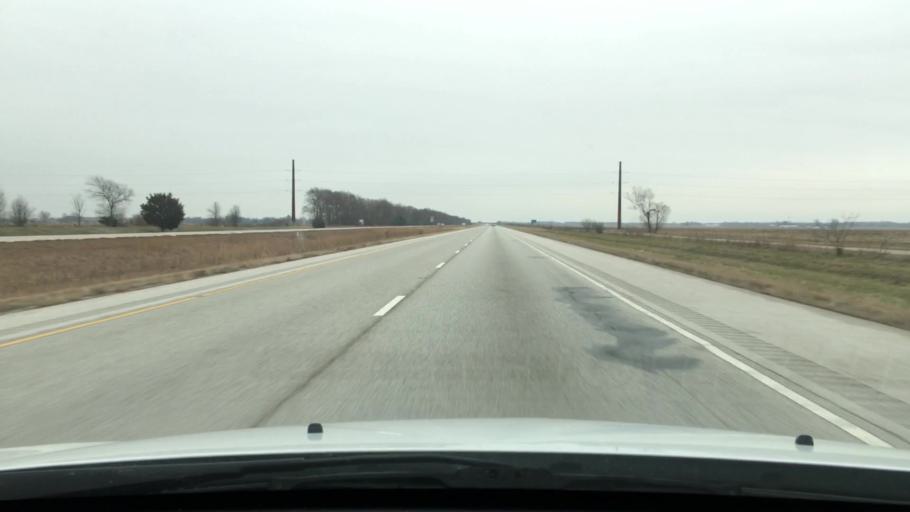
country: US
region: Illinois
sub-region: Scott County
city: Winchester
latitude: 39.6801
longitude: -90.3764
